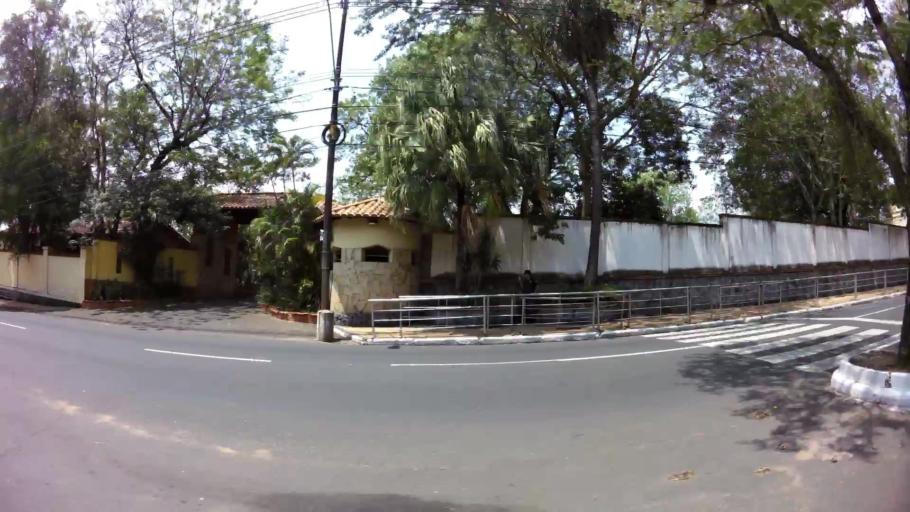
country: PY
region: Asuncion
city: Asuncion
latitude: -25.2951
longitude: -57.6040
